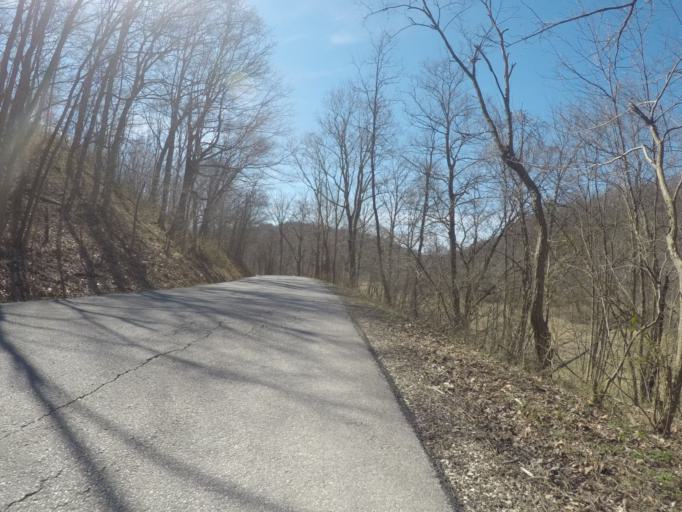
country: US
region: Ohio
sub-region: Lawrence County
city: South Point
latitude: 38.4685
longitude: -82.5685
